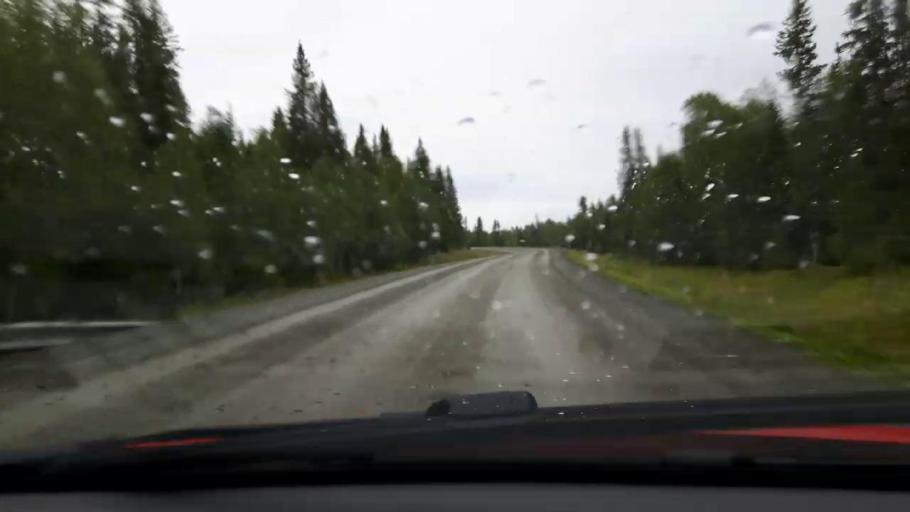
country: SE
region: Jaemtland
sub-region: Are Kommun
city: Are
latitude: 63.4702
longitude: 12.5959
